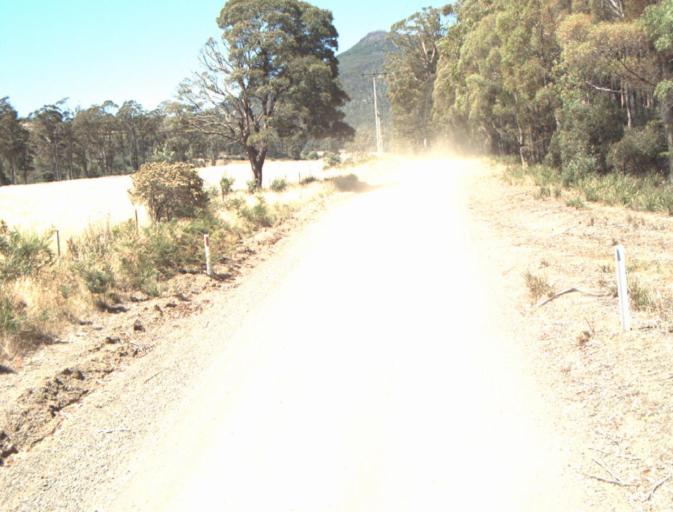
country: AU
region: Tasmania
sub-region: Launceston
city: Newstead
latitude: -41.3451
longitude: 147.3709
